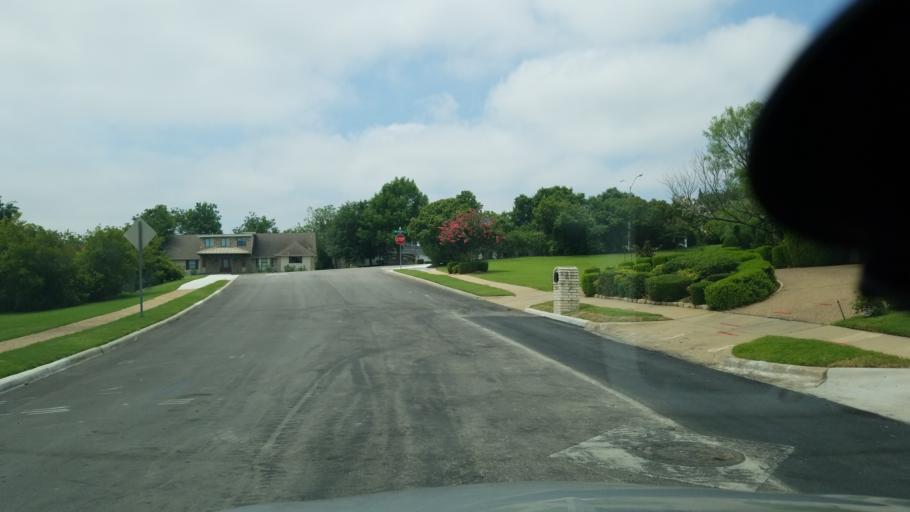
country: US
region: Texas
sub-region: Dallas County
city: Irving
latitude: 32.8518
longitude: -96.9402
